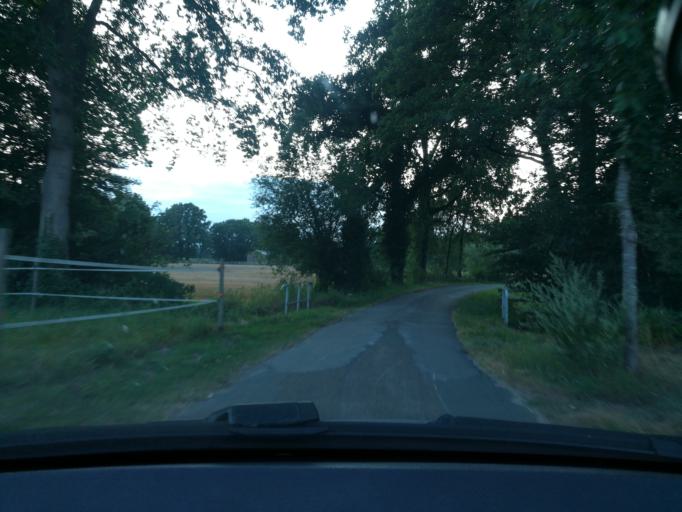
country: DE
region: North Rhine-Westphalia
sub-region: Regierungsbezirk Munster
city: Lienen
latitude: 52.1322
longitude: 7.9836
